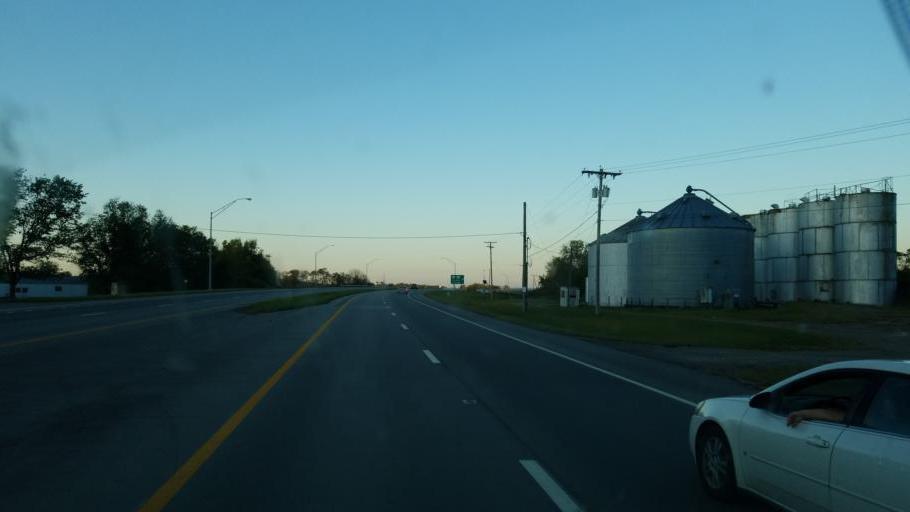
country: US
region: Ohio
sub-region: Pike County
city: Piketon
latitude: 39.0418
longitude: -83.0274
